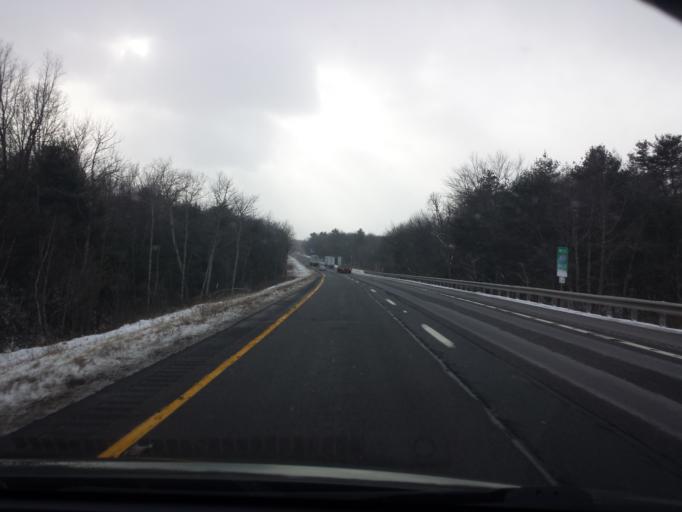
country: US
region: Pennsylvania
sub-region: Luzerne County
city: White Haven
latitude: 41.0743
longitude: -75.6796
